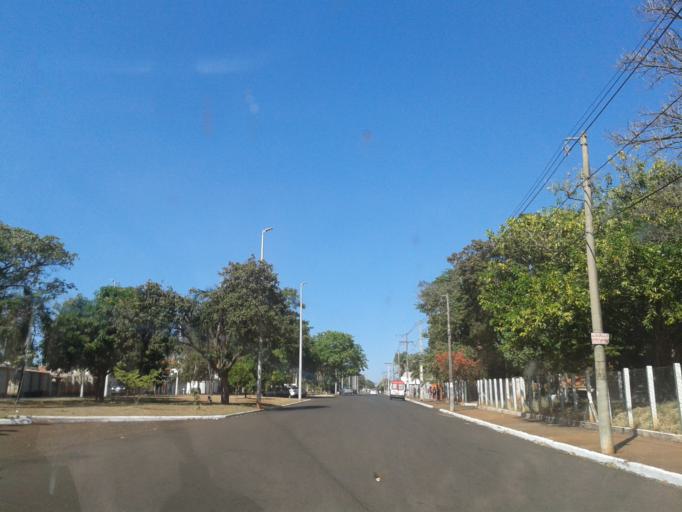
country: BR
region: Minas Gerais
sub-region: Ituiutaba
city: Ituiutaba
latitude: -18.9836
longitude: -49.4629
